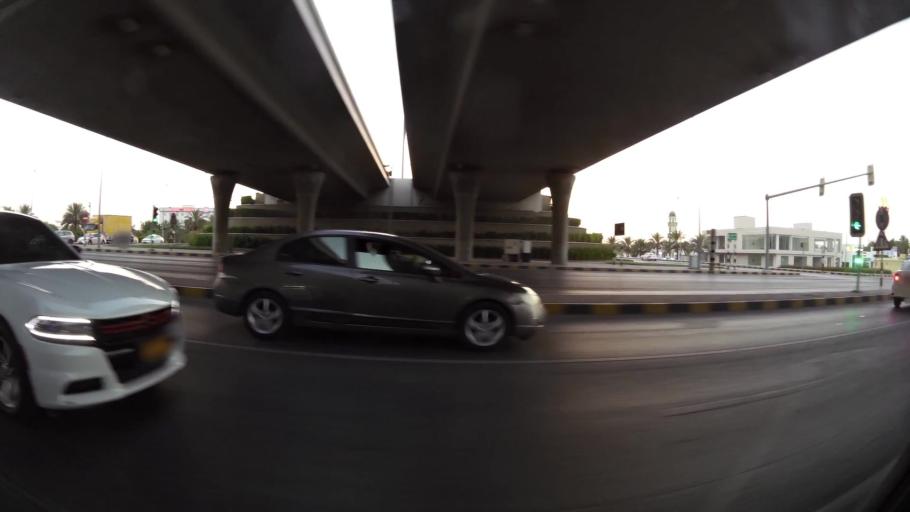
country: OM
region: Muhafazat Masqat
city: As Sib al Jadidah
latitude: 23.6548
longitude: 58.2059
